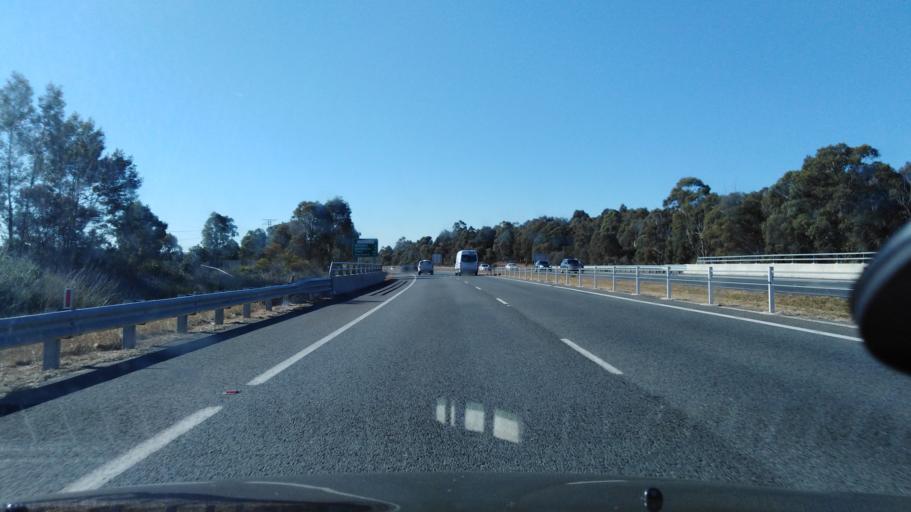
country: AU
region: Australian Capital Territory
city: Kaleen
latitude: -35.2375
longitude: 149.1142
